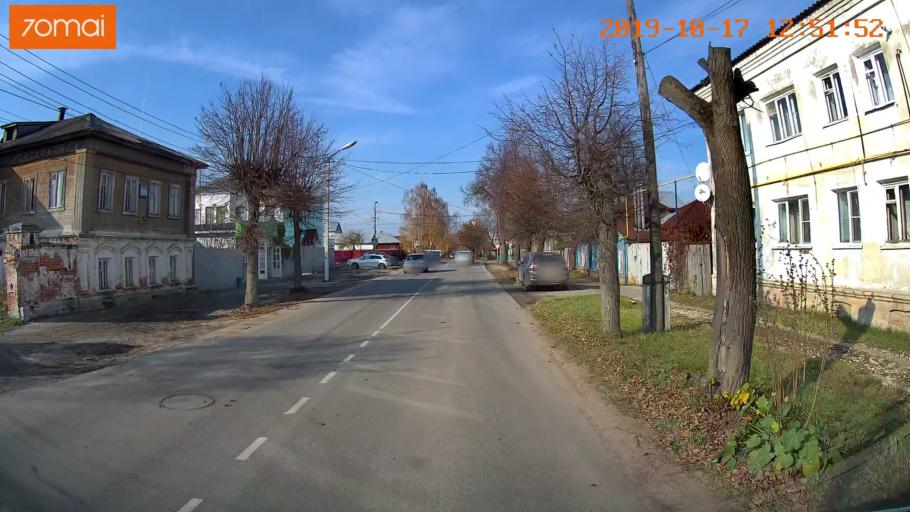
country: RU
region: Rjazan
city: Kasimov
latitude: 54.9422
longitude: 41.3898
